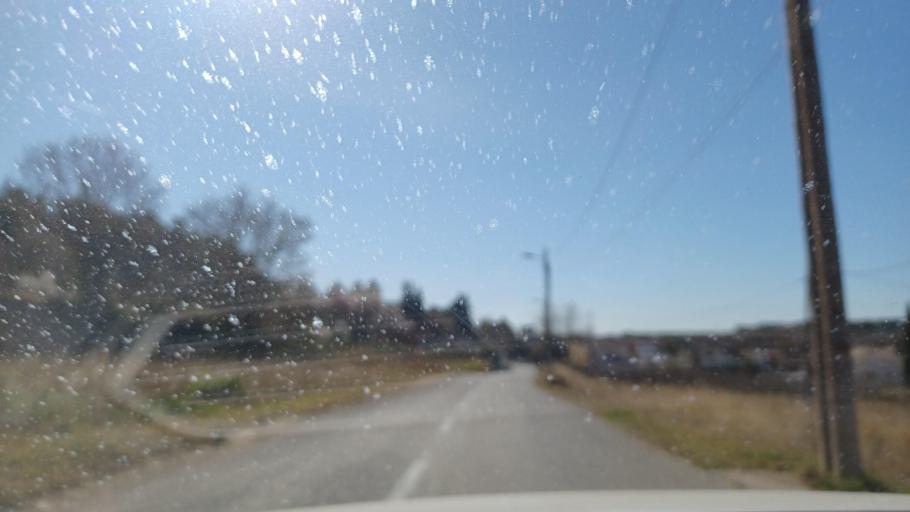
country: ES
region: Catalonia
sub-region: Provincia de Barcelona
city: Vilafranca del Penedes
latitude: 41.3574
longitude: 1.6715
